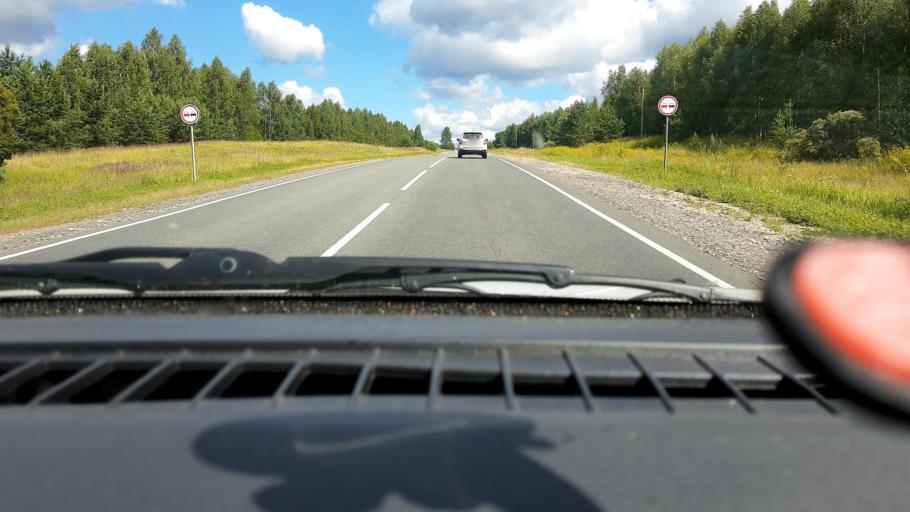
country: RU
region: Nizjnij Novgorod
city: Arzamas
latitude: 55.3469
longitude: 43.8917
